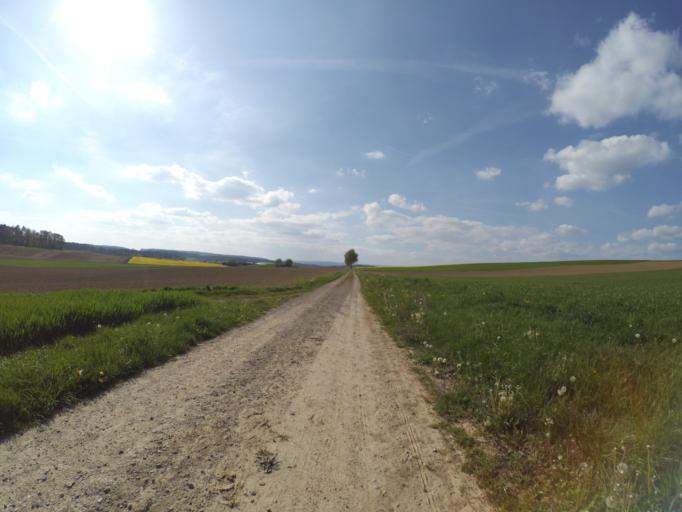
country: CH
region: Thurgau
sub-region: Frauenfeld District
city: Diessenhofen
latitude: 47.6600
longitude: 8.7607
